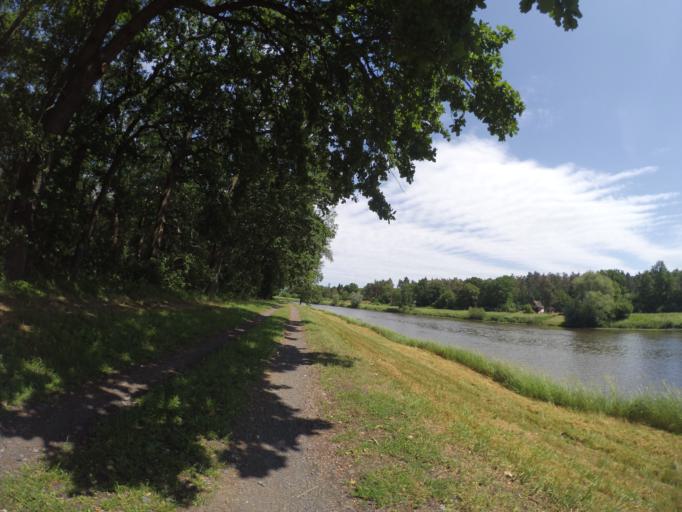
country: CZ
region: Central Bohemia
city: Poricany
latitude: 50.1656
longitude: 14.9146
